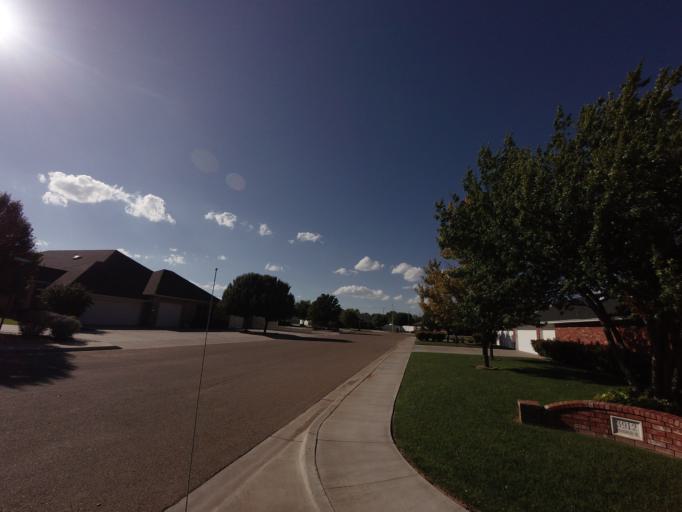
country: US
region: New Mexico
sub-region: Curry County
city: Clovis
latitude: 34.4401
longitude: -103.1770
